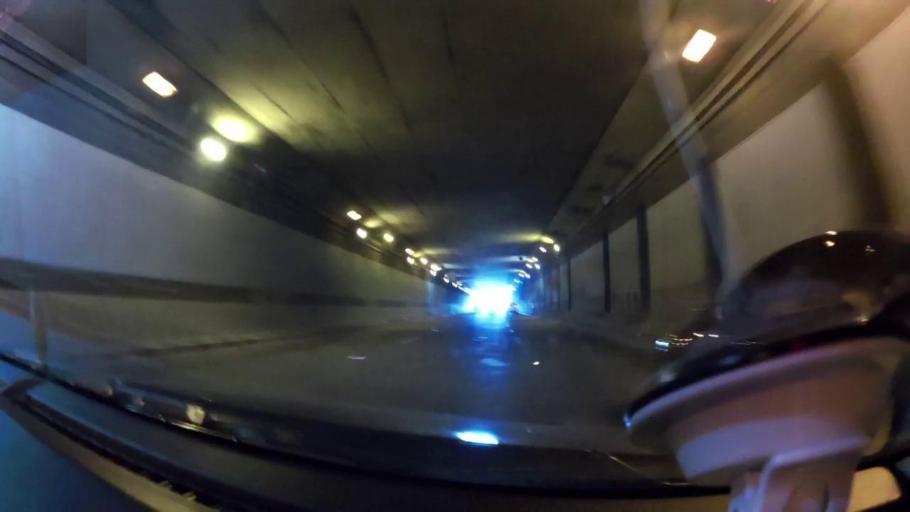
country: TH
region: Prachuap Khiri Khan
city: Hua Hin
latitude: 12.6423
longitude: 99.9490
